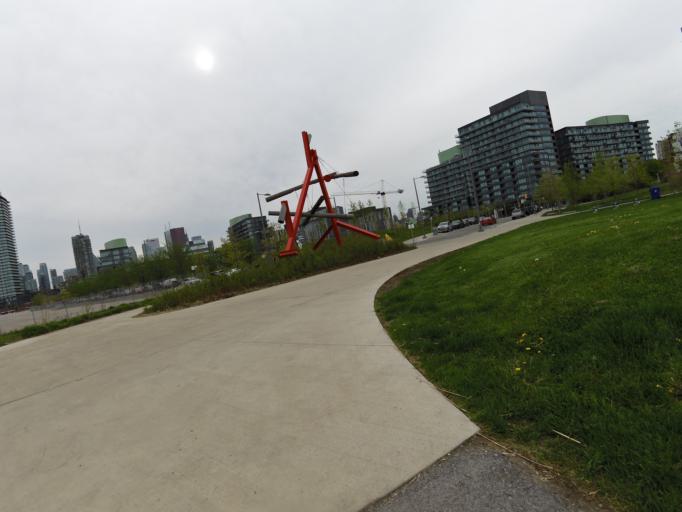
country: CA
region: Ontario
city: Toronto
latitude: 43.6527
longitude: -79.3526
